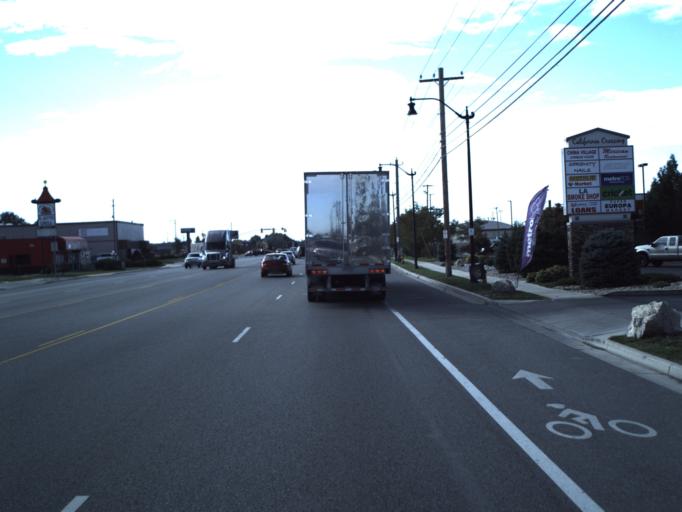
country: US
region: Utah
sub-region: Salt Lake County
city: Salt Lake City
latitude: 40.7429
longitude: -111.9391
